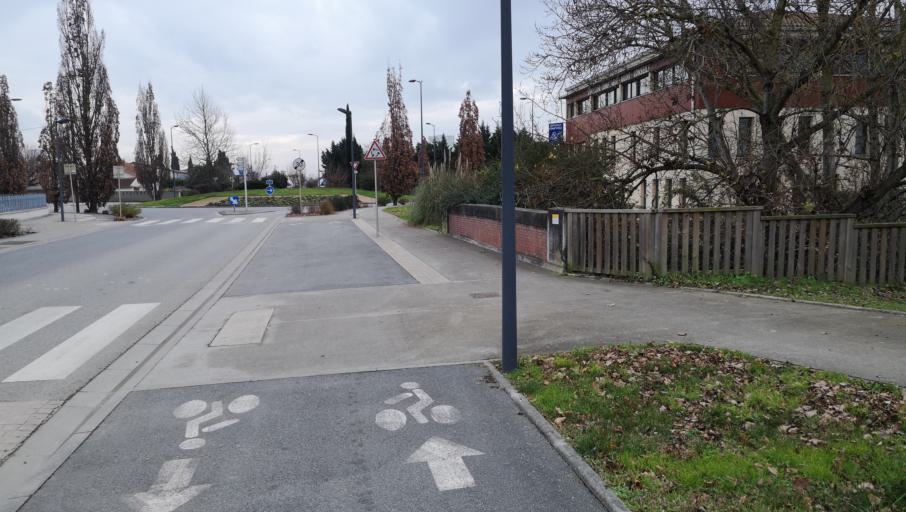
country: FR
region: Midi-Pyrenees
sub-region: Departement de la Haute-Garonne
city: Beauzelle
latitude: 43.6507
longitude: 1.3813
